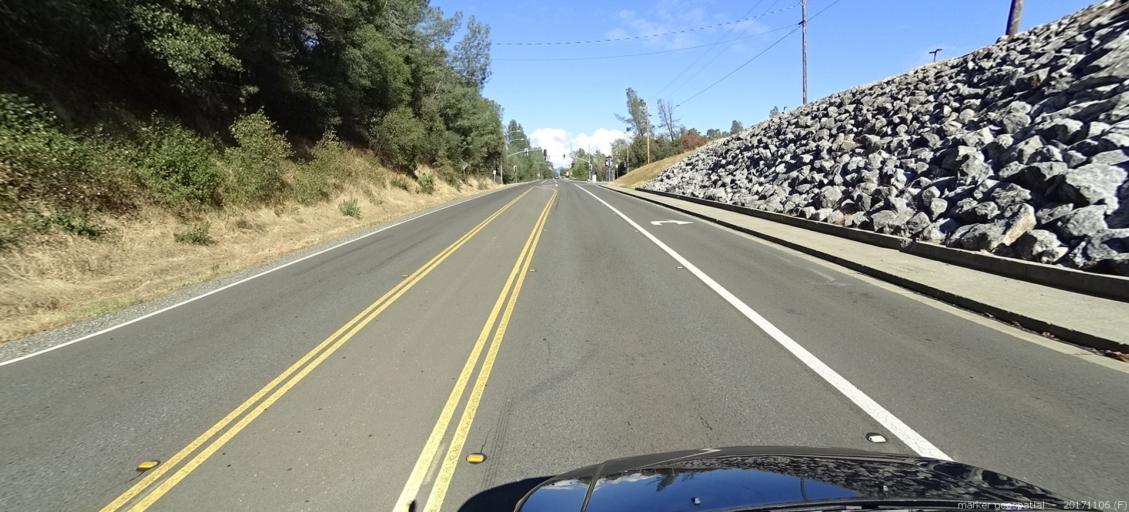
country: US
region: California
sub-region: Shasta County
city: Palo Cedro
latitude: 40.5695
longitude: -122.2386
